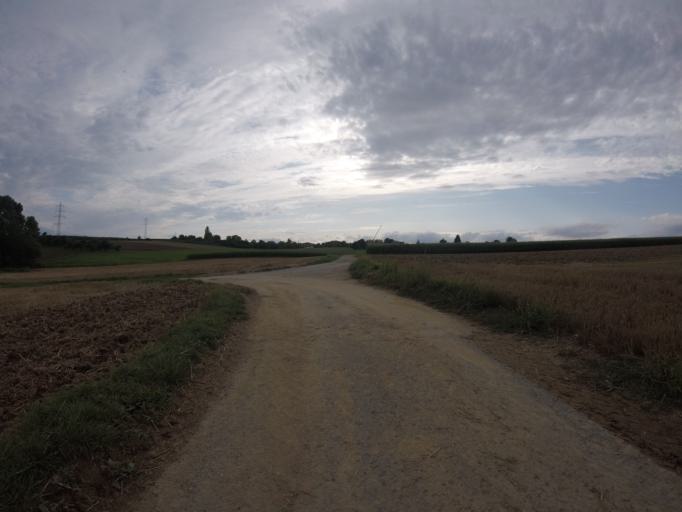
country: DE
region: Baden-Wuerttemberg
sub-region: Regierungsbezirk Stuttgart
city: Backnang
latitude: 48.9351
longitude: 9.4547
